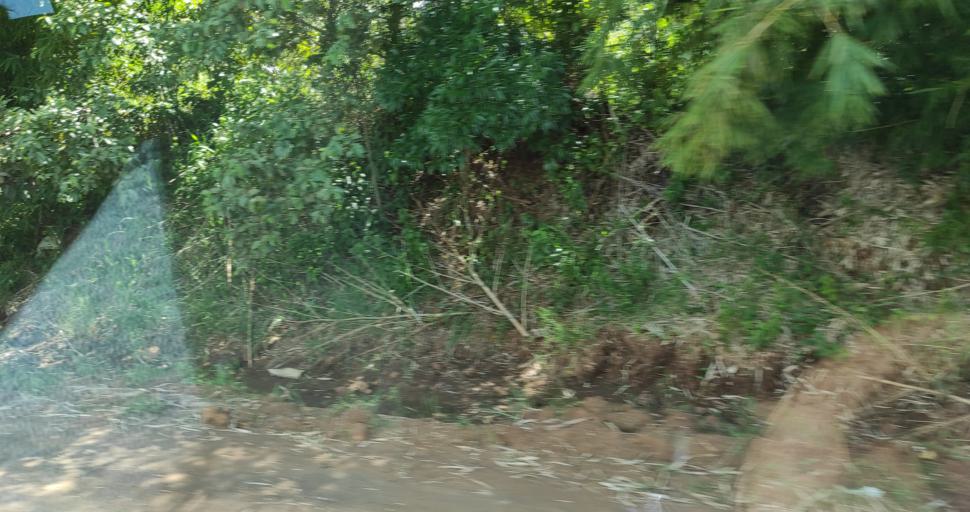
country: AR
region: Misiones
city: El Soberbio
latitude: -27.2867
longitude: -54.1988
